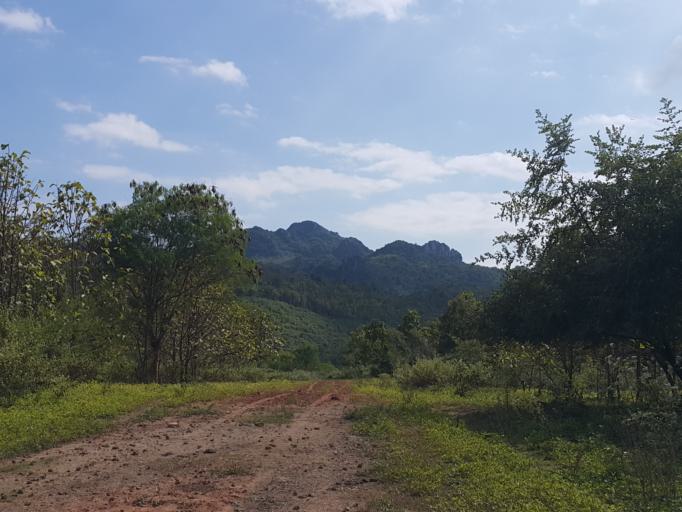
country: TH
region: Lampang
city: Mae Mo
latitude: 18.3431
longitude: 99.7653
